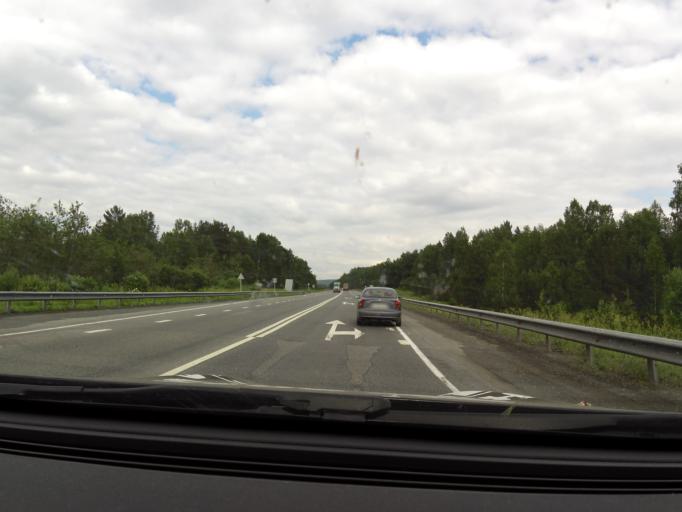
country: RU
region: Sverdlovsk
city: Druzhinino
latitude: 56.8322
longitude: 59.6275
